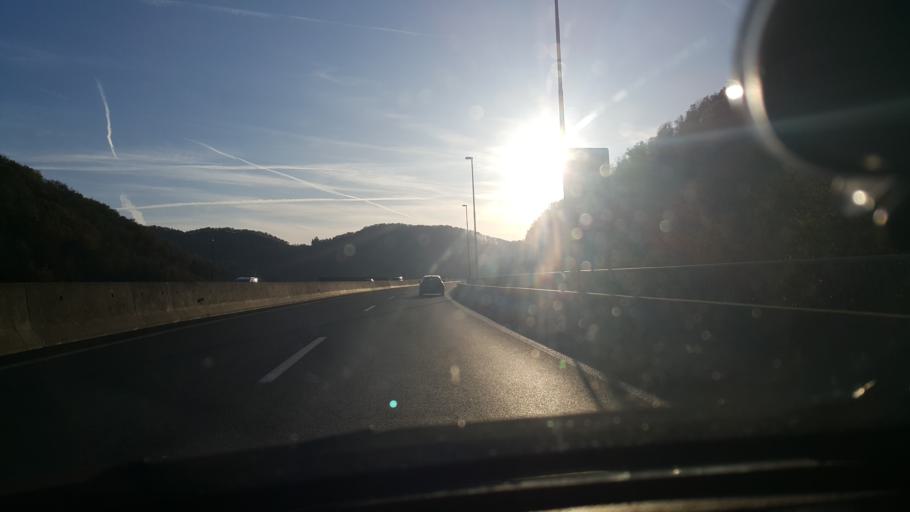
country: SI
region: Slovenska Konjice
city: Slovenske Konjice
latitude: 46.3101
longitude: 15.4552
